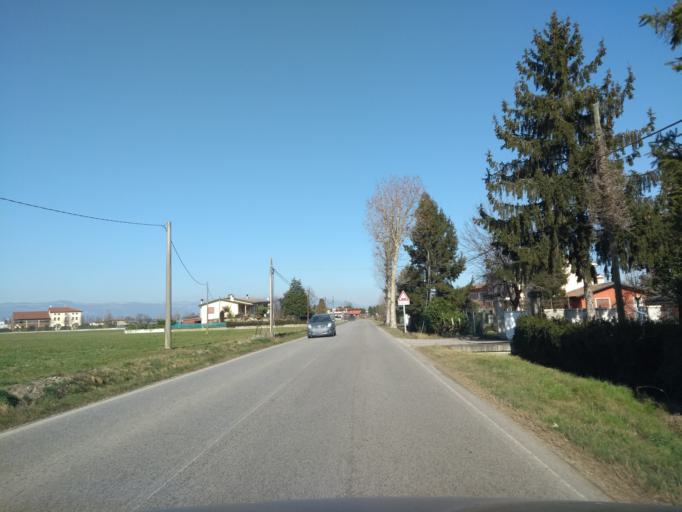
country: IT
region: Veneto
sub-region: Provincia di Vicenza
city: Bolzano Vicentino
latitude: 45.5939
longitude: 11.6368
